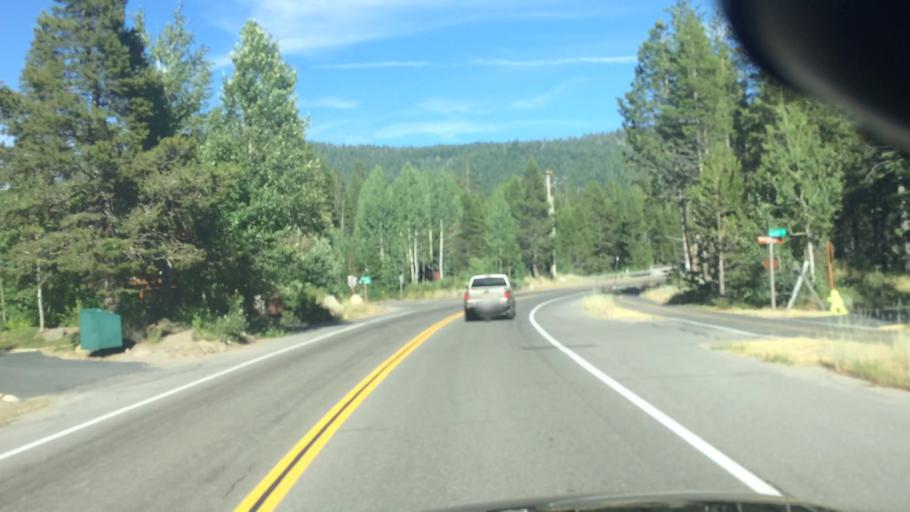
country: US
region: California
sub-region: Placer County
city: Sunnyside-Tahoe City
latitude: 39.2072
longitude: -120.2118
